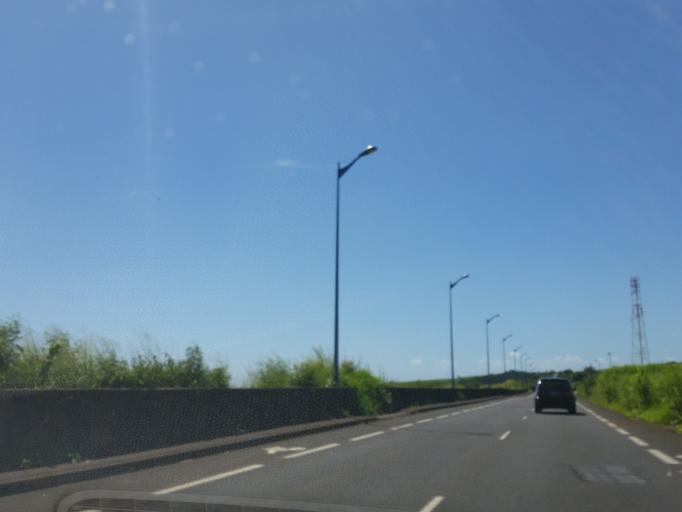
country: RE
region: Reunion
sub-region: Reunion
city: Sainte-Marie
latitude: -20.9115
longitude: 55.5140
